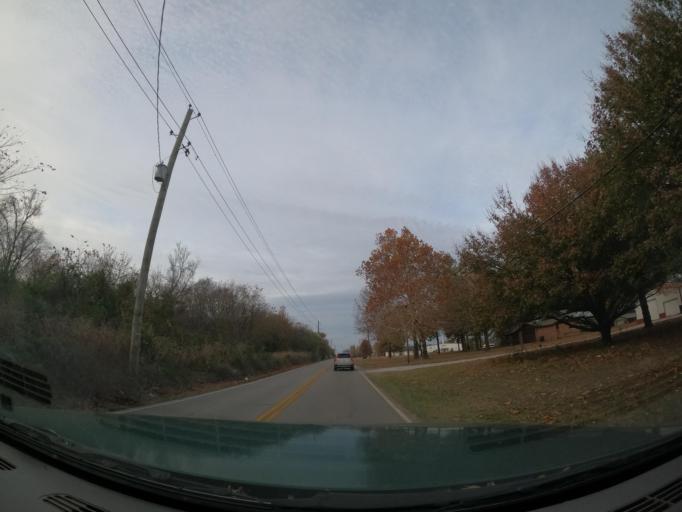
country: US
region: Oklahoma
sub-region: Tulsa County
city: Broken Arrow
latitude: 35.9828
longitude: -95.8153
